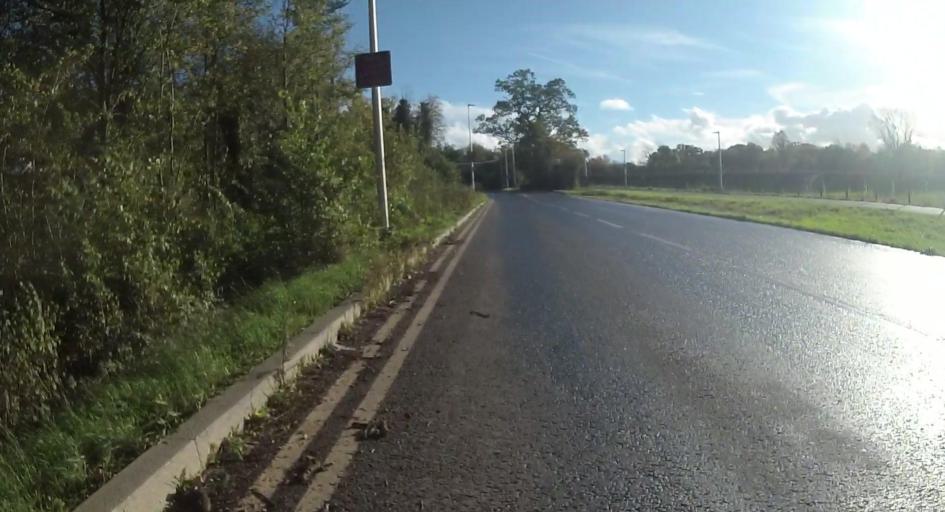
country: GB
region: England
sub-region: Wokingham
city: Wokingham
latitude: 51.4225
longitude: -0.8335
